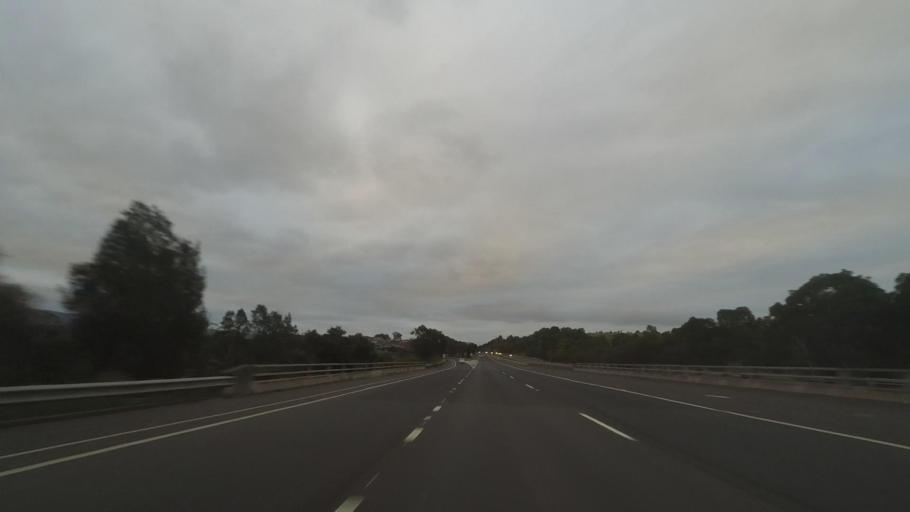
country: AU
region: New South Wales
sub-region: Wollongong
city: Dapto
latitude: -34.5269
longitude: 150.7871
